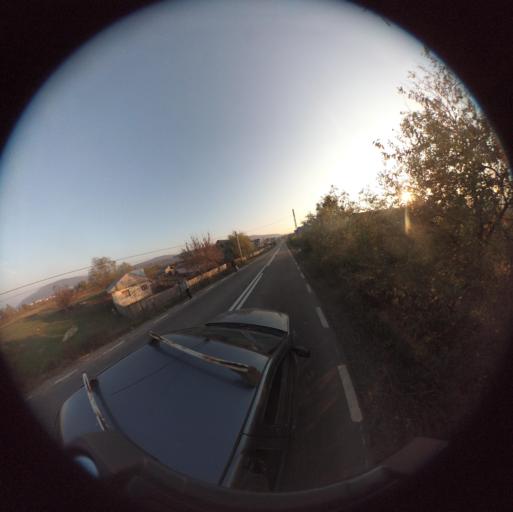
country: RO
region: Vaslui
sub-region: Comuna Bacesti
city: Bacesti
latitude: 46.8299
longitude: 27.2515
